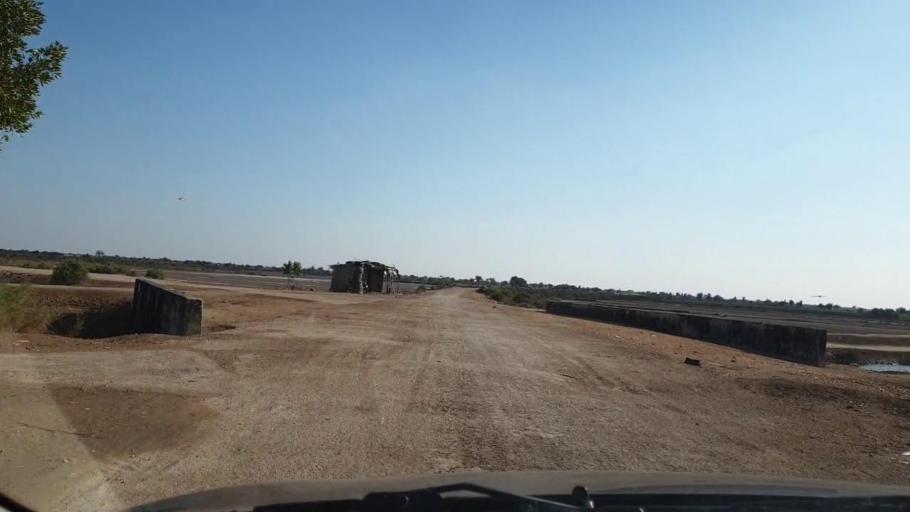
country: PK
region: Sindh
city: Sinjhoro
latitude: 26.0055
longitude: 68.8390
